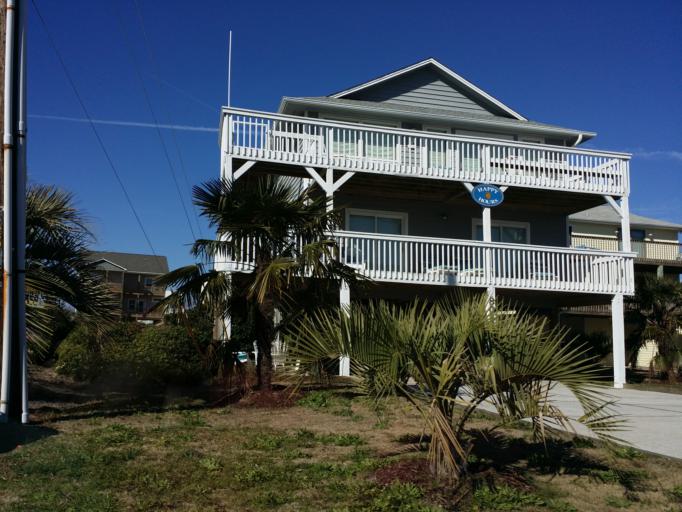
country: US
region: North Carolina
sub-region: Pender County
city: Surf City
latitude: 34.4206
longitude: -77.5536
